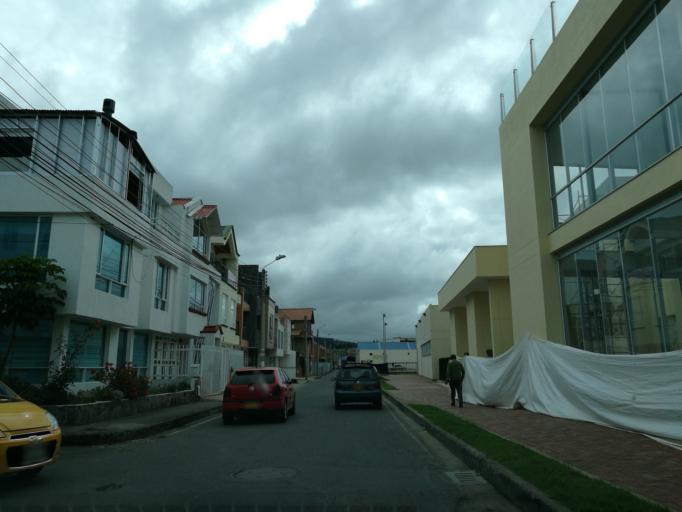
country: CO
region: Boyaca
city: Tunja
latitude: 5.5483
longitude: -73.3580
